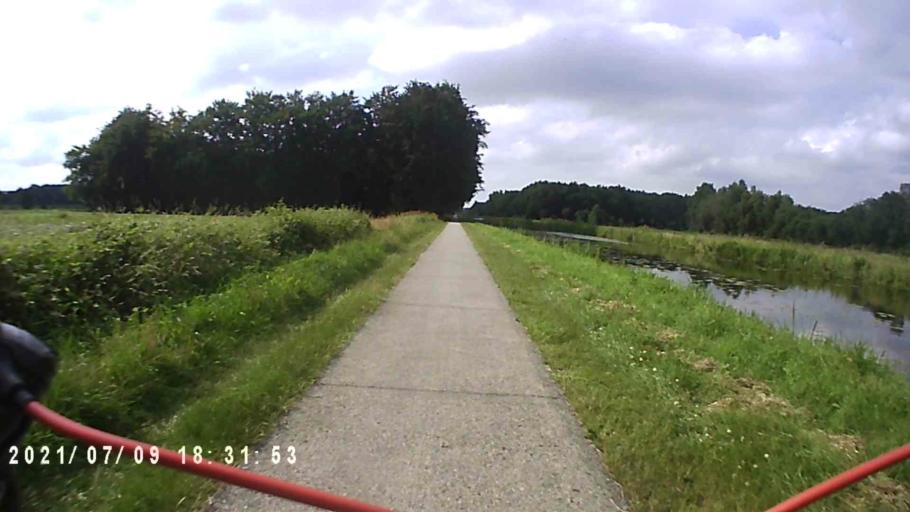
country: NL
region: Groningen
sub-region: Gemeente Pekela
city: Oude Pekela
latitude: 53.0696
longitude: 6.9729
